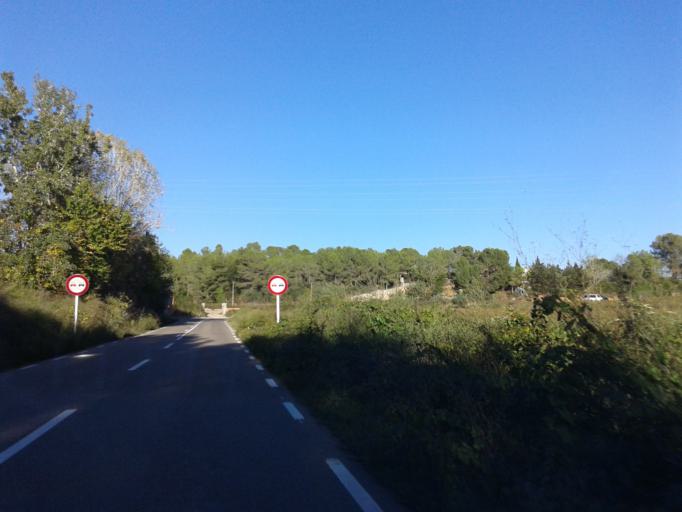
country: ES
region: Catalonia
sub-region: Provincia de Barcelona
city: Avinyonet del Penedes
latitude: 41.3176
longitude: 1.7606
